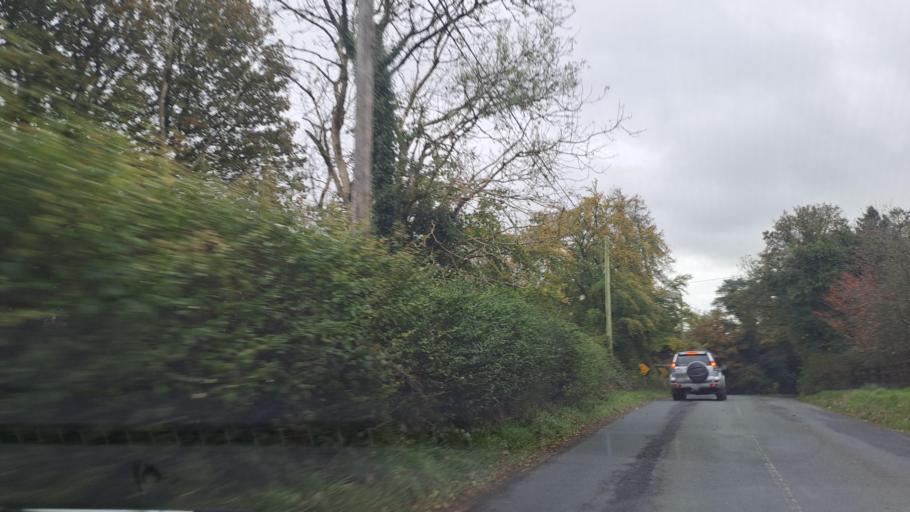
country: IE
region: Ulster
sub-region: An Cabhan
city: Bailieborough
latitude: 53.9475
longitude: -7.0257
